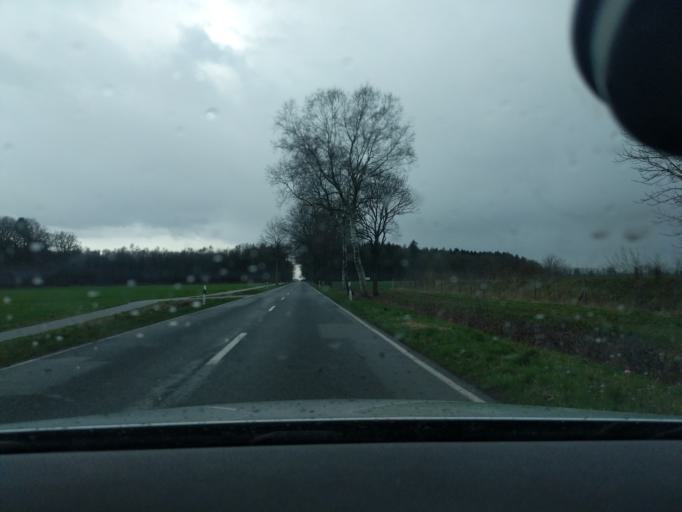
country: DE
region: Lower Saxony
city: Harsefeld
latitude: 53.4789
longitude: 9.5026
